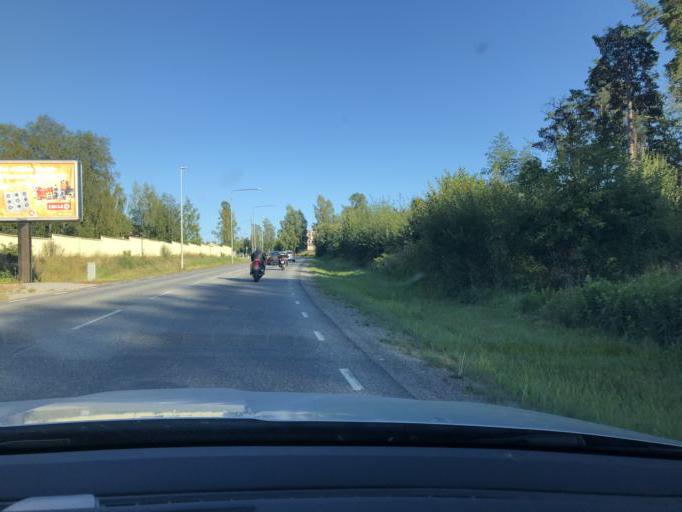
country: SE
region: Stockholm
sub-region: Sodertalje Kommun
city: Soedertaelje
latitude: 59.1843
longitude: 17.5922
